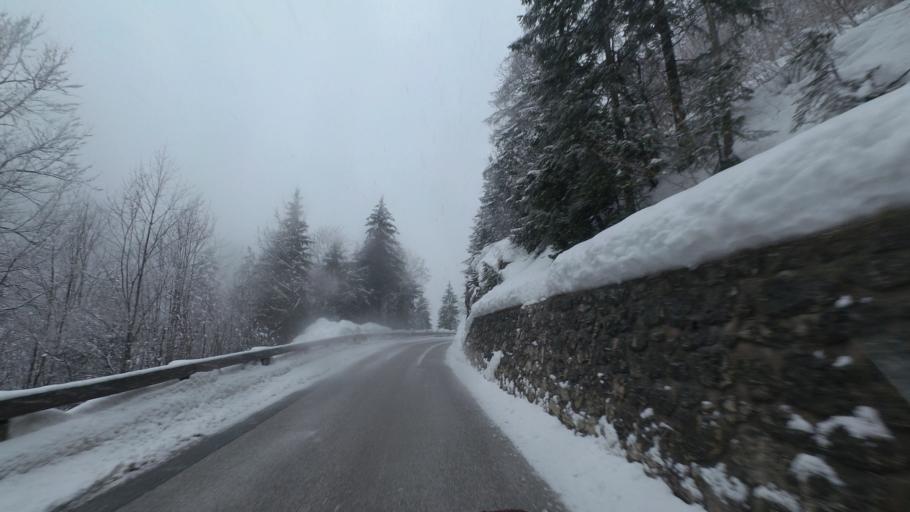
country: AT
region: Tyrol
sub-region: Politischer Bezirk Kitzbuhel
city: Kossen
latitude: 47.6859
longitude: 12.3968
